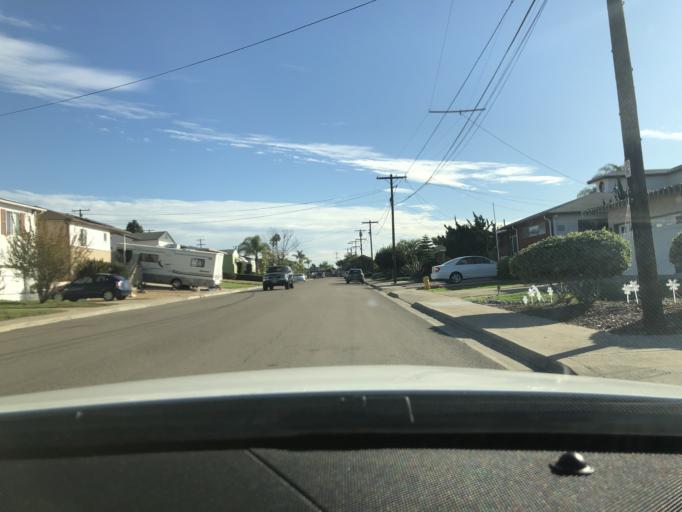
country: US
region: California
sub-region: San Diego County
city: Lemon Grove
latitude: 32.7550
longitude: -117.0717
